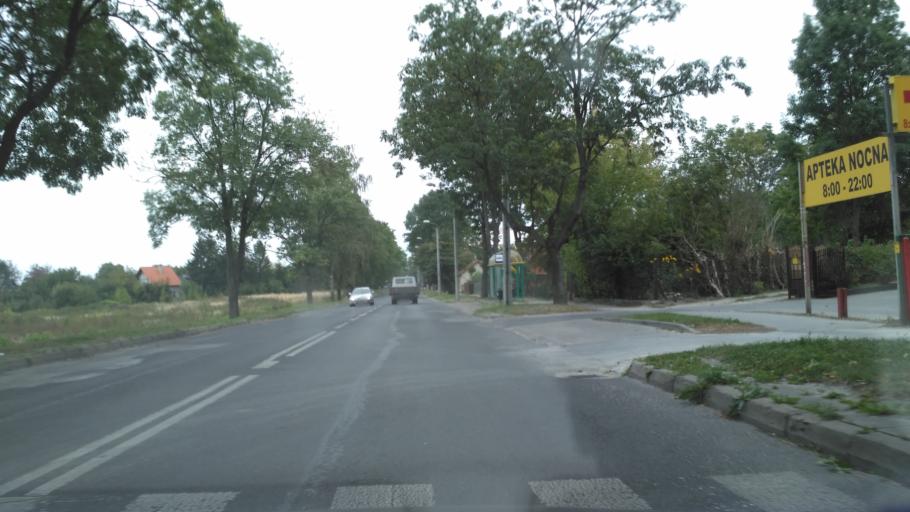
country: PL
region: Lublin Voivodeship
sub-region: Chelm
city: Chelm
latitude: 51.1440
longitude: 23.4435
